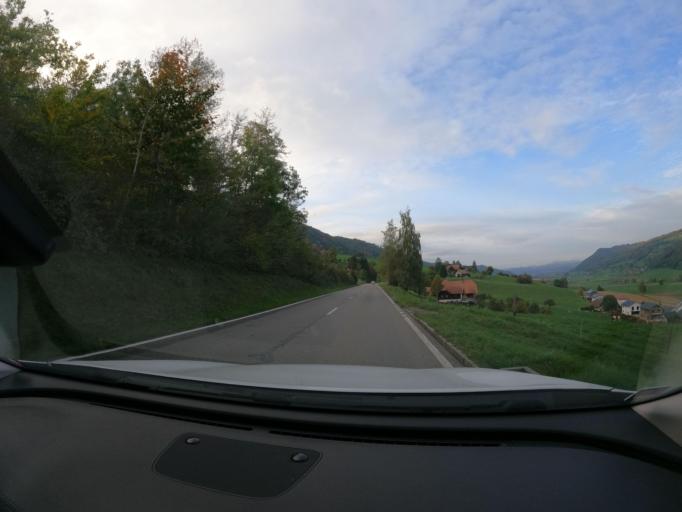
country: CH
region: Bern
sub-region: Bern-Mittelland District
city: Hermiswil
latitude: 46.8373
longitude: 7.4934
